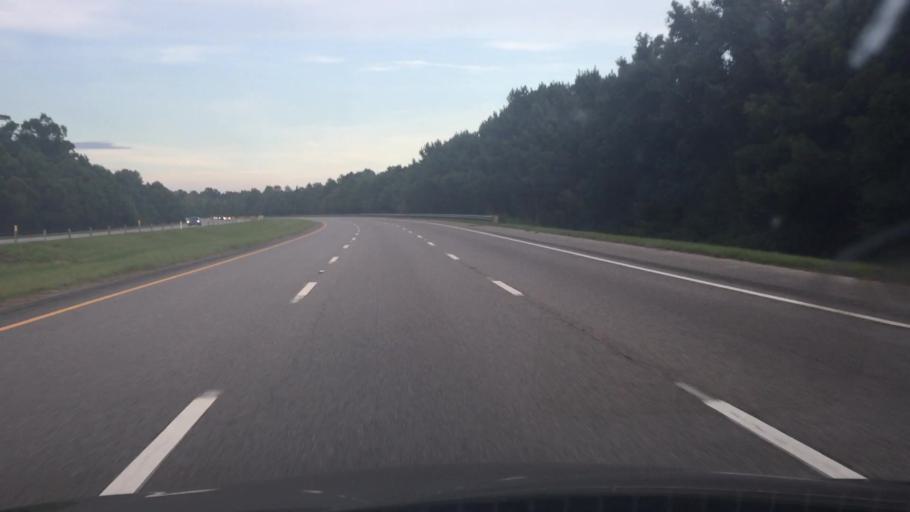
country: US
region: South Carolina
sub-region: Horry County
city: Myrtle Beach
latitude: 33.7491
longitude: -78.8862
